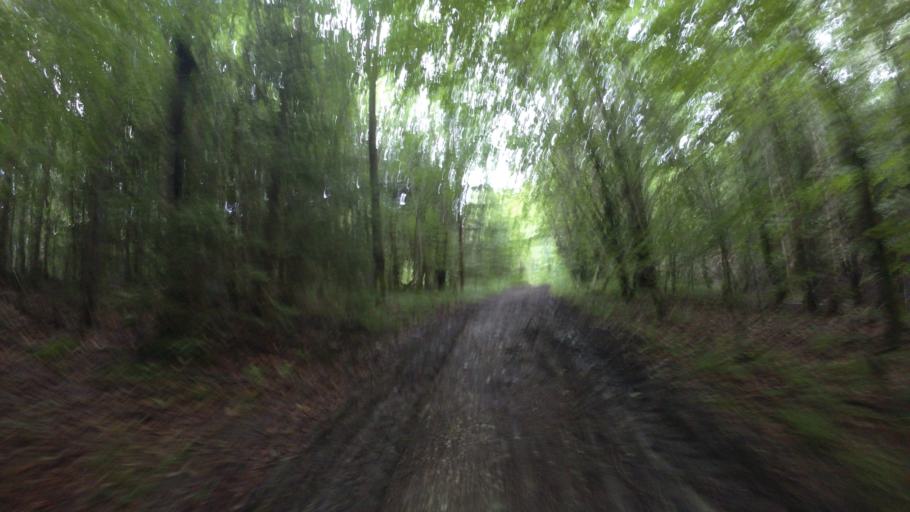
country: DE
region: Bavaria
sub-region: Upper Bavaria
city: Grabenstatt
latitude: 47.8354
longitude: 12.5386
